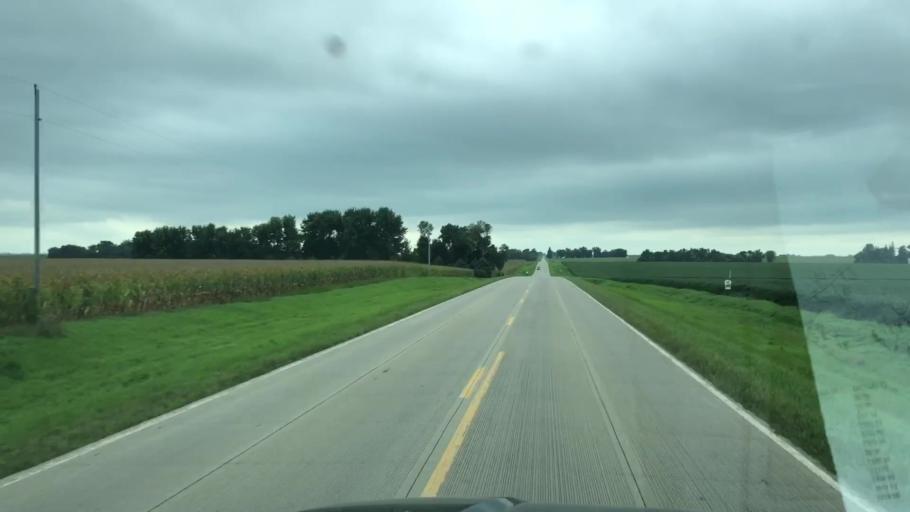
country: US
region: Iowa
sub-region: O'Brien County
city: Sheldon
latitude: 43.1223
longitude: -95.9789
